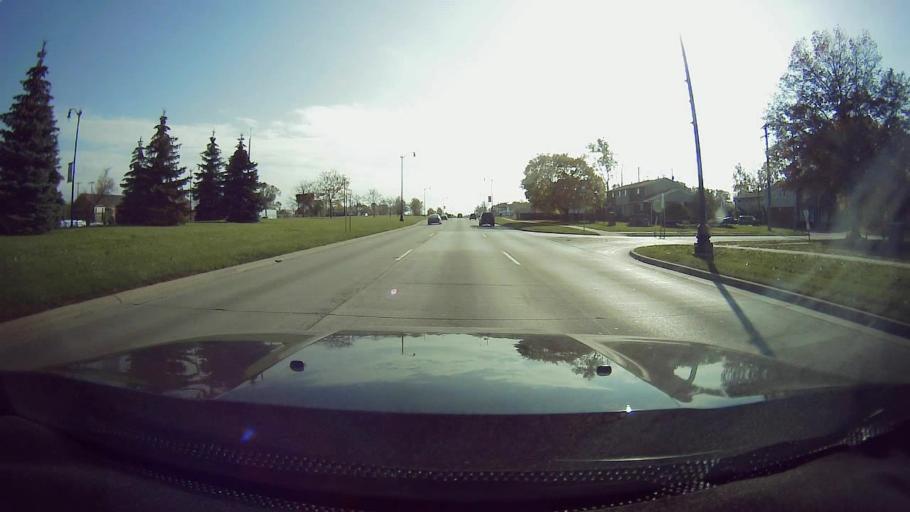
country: US
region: Michigan
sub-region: Wayne County
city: Taylor
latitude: 42.2201
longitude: -83.2692
